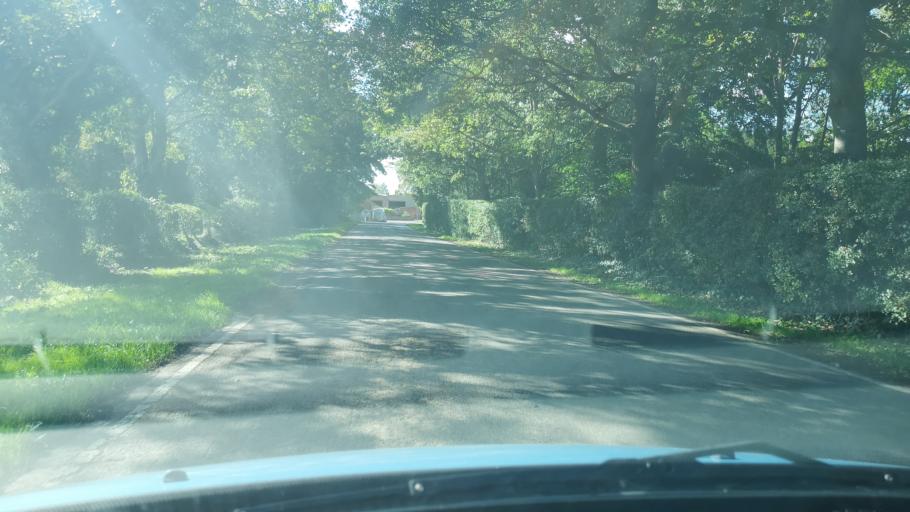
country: GB
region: England
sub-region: North Lincolnshire
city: Eastoft
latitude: 53.6359
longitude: -0.7806
